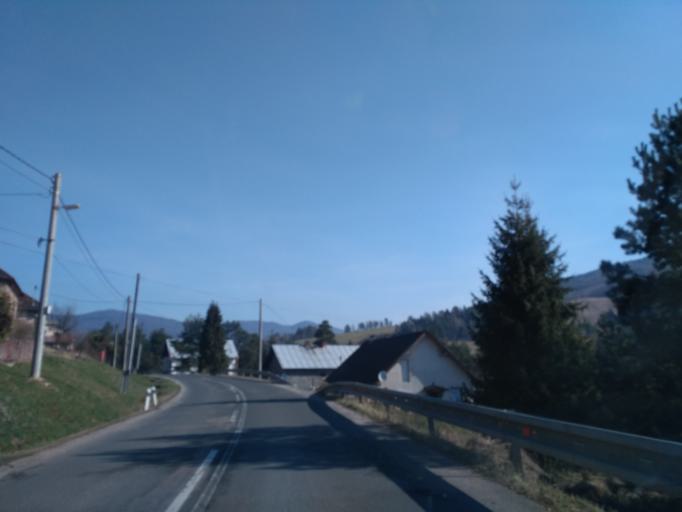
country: SK
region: Kosicky
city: Medzev
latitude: 48.7937
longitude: 20.8062
